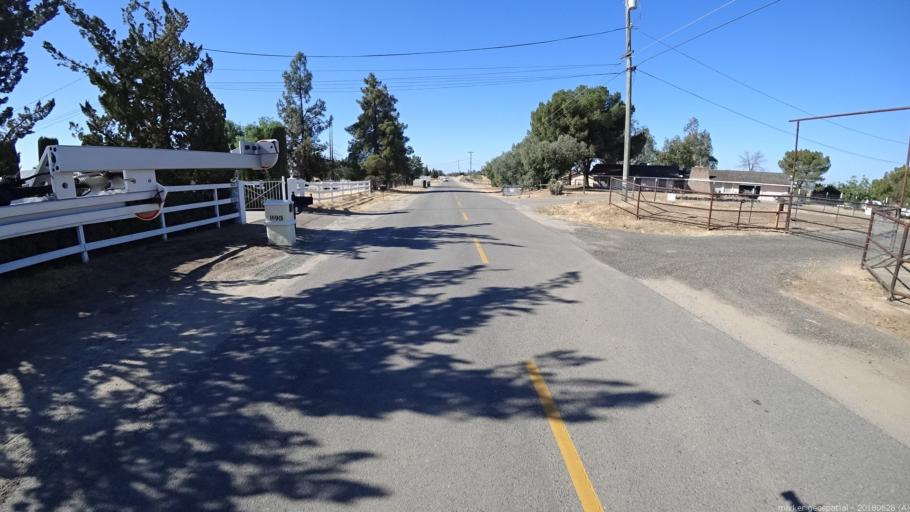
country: US
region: California
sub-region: Madera County
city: Bonadelle Ranchos-Madera Ranchos
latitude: 36.9942
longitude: -119.8901
